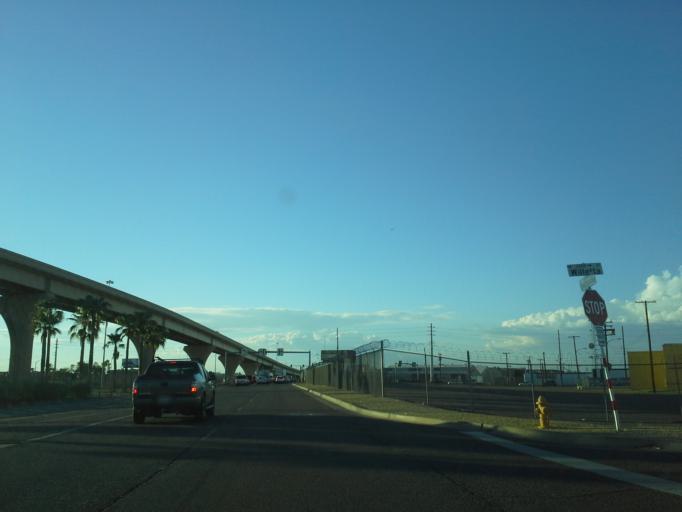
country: US
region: Arizona
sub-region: Maricopa County
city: Phoenix
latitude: 33.4639
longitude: -112.1078
